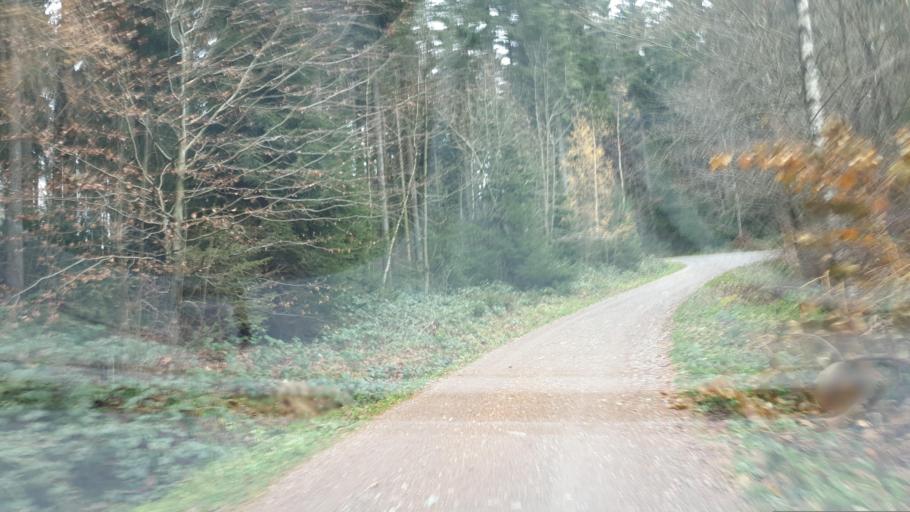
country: DE
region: Saxony
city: Dorfchemnitz
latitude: 50.7832
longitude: 13.4355
